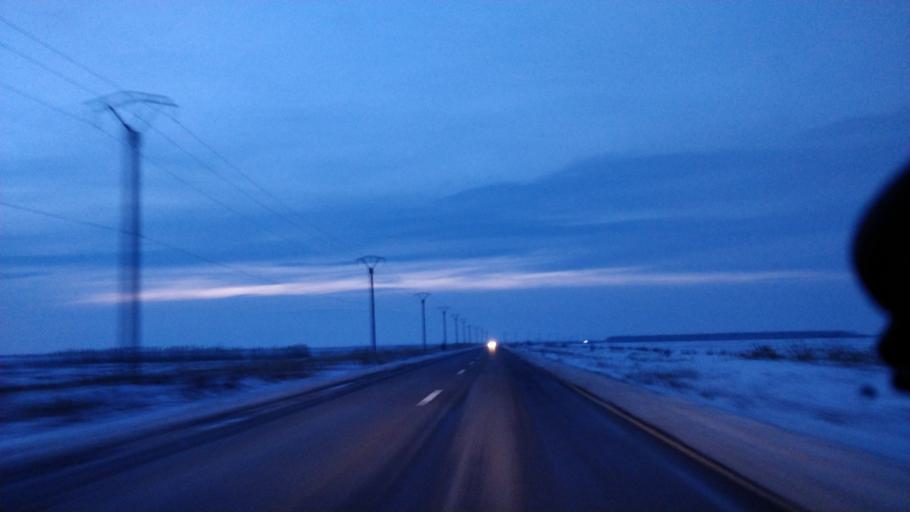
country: RO
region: Vrancea
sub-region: Comuna Vulturu
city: Vadu Rosca
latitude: 45.5937
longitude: 27.4742
